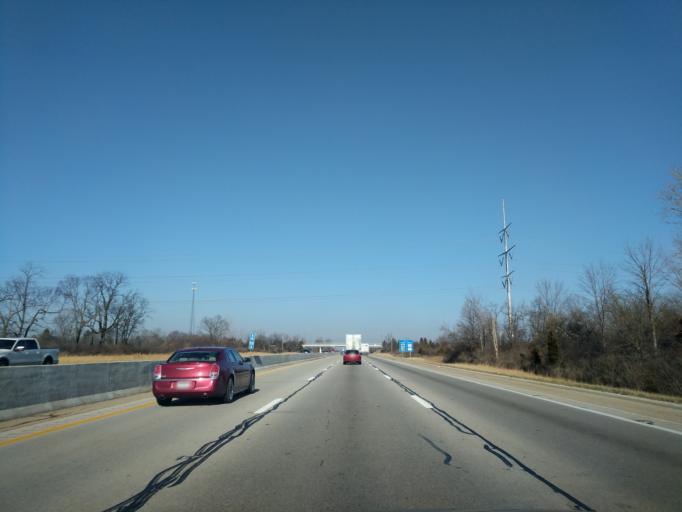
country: US
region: Ohio
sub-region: Miami County
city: Tipp City
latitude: 39.9411
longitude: -84.1889
